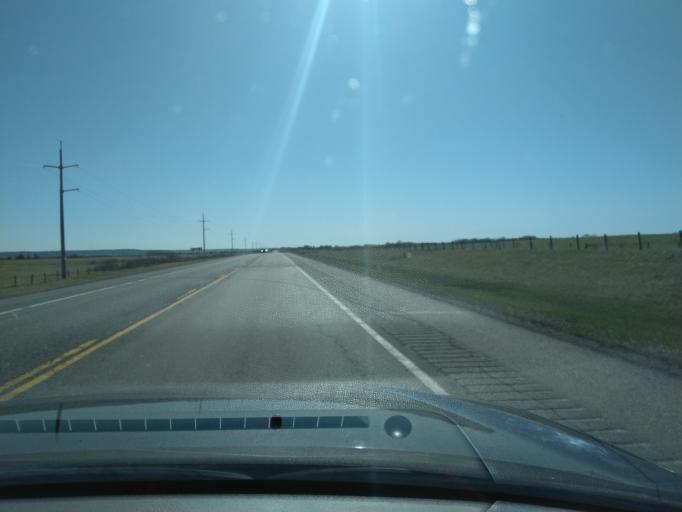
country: CA
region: Alberta
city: Cochrane
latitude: 51.0233
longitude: -114.4191
